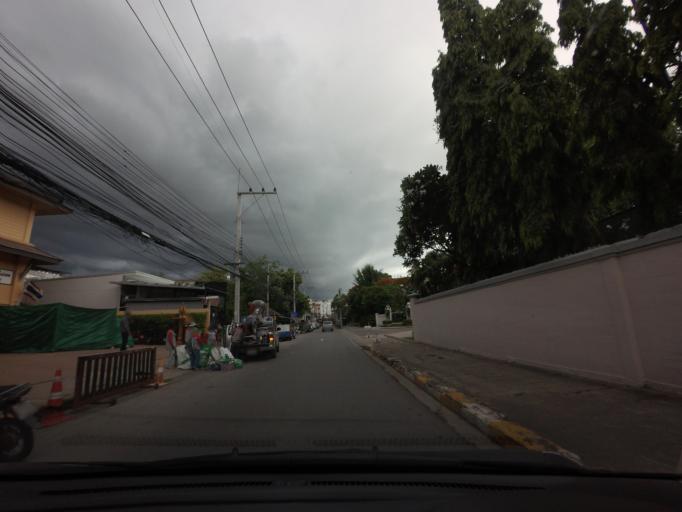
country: TH
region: Prachuap Khiri Khan
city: Hua Hin
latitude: 12.5673
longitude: 99.9601
